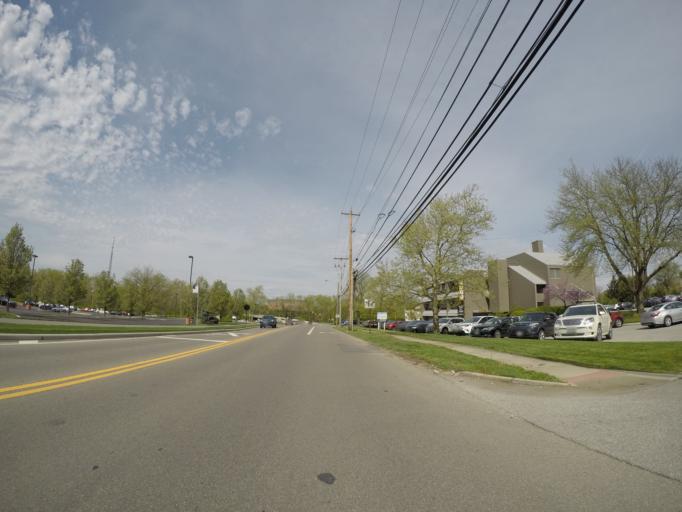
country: US
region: Ohio
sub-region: Franklin County
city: Upper Arlington
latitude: 39.9897
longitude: -83.0649
